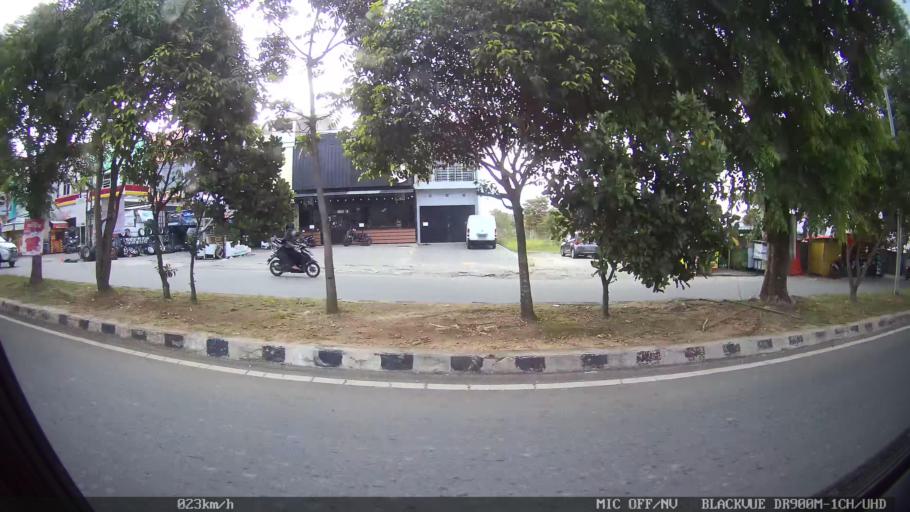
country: ID
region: Lampung
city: Kedaton
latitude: -5.3991
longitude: 105.2117
